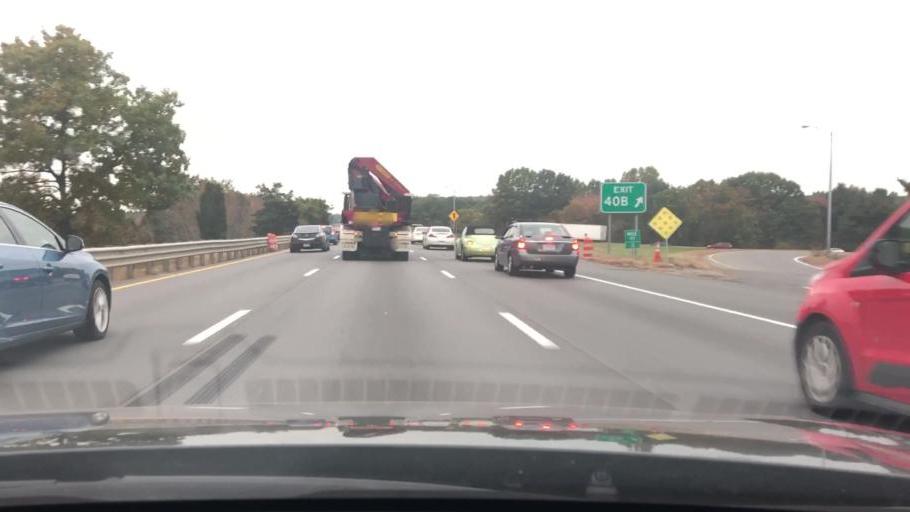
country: US
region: Massachusetts
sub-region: Essex County
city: Lawrence
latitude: 42.6669
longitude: -71.1911
